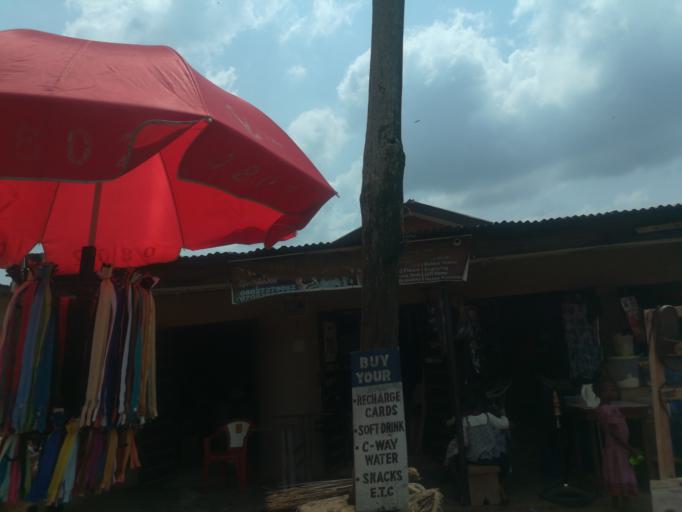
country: NG
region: Oyo
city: Moniya
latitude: 7.4552
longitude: 3.9619
